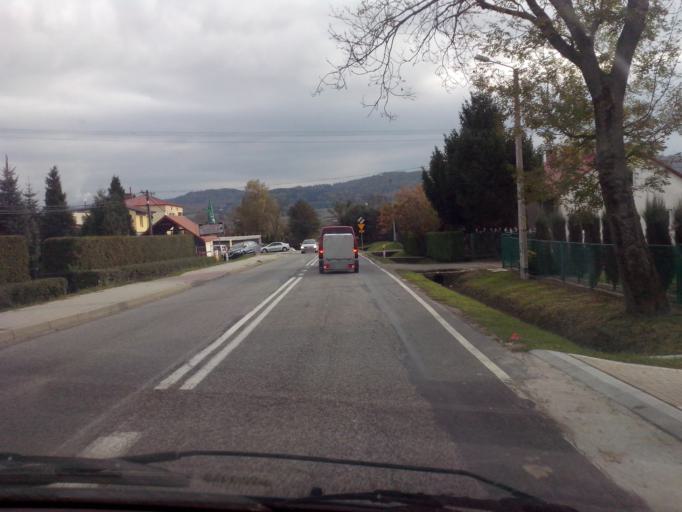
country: PL
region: Subcarpathian Voivodeship
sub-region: Powiat strzyzowski
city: Wisniowa
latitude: 49.8705
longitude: 21.6598
